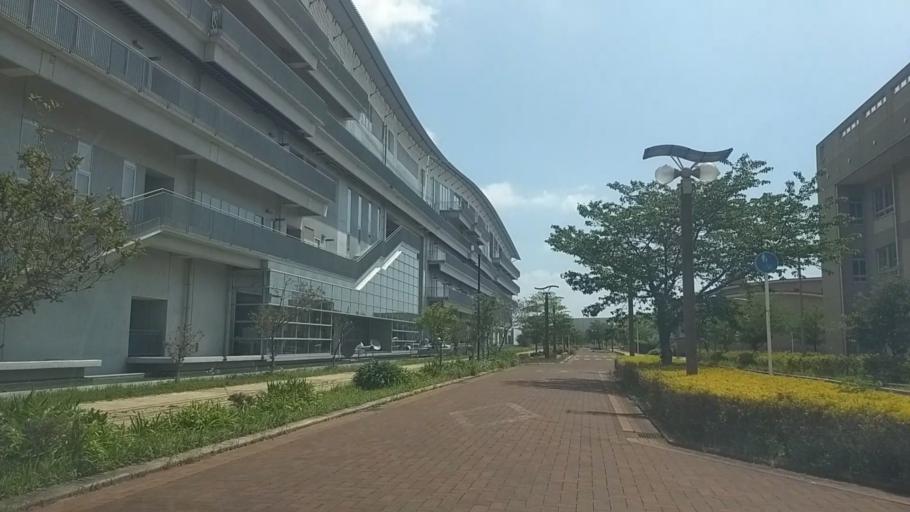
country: JP
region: Shizuoka
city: Hamamatsu
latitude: 34.7123
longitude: 137.7385
